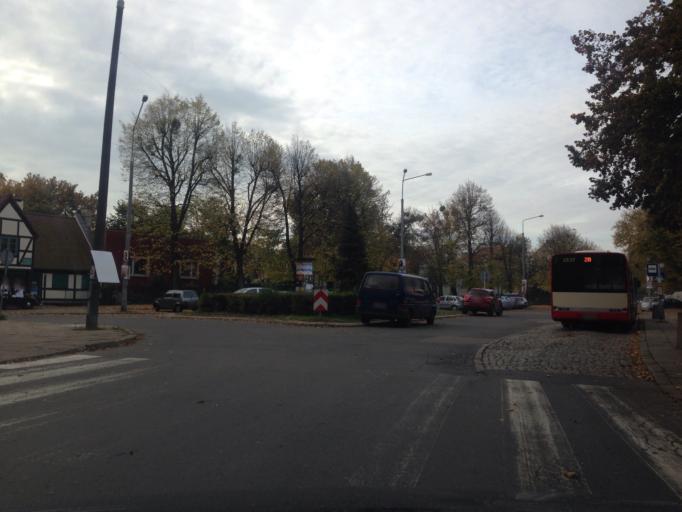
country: PL
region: Pomeranian Voivodeship
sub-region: Gdansk
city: Gdansk
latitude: 54.3232
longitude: 18.6325
